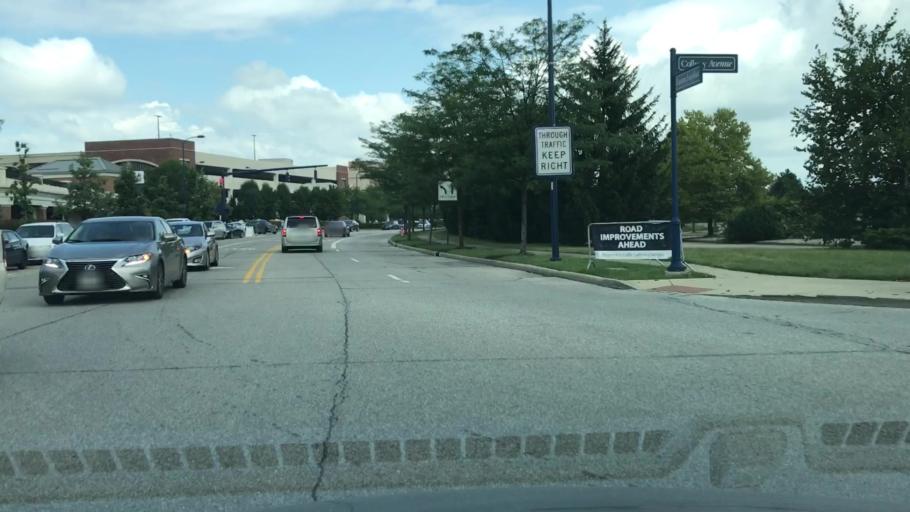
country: US
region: Ohio
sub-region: Franklin County
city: Huber Ridge
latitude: 40.0507
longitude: -82.9115
